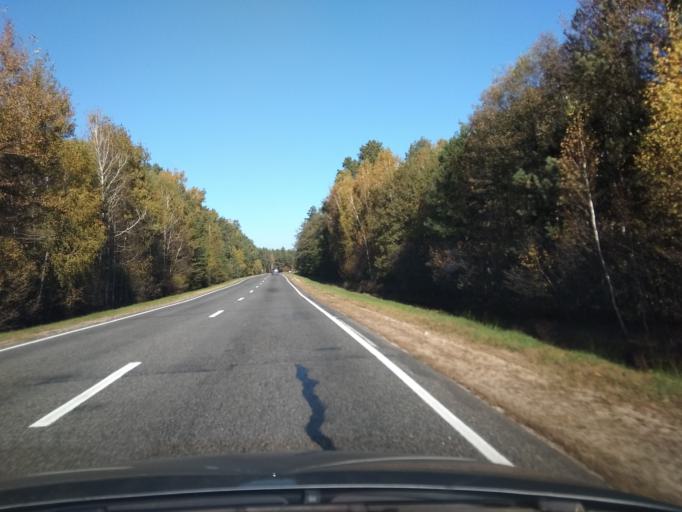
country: BY
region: Brest
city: Kobryn
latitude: 52.0945
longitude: 24.2783
